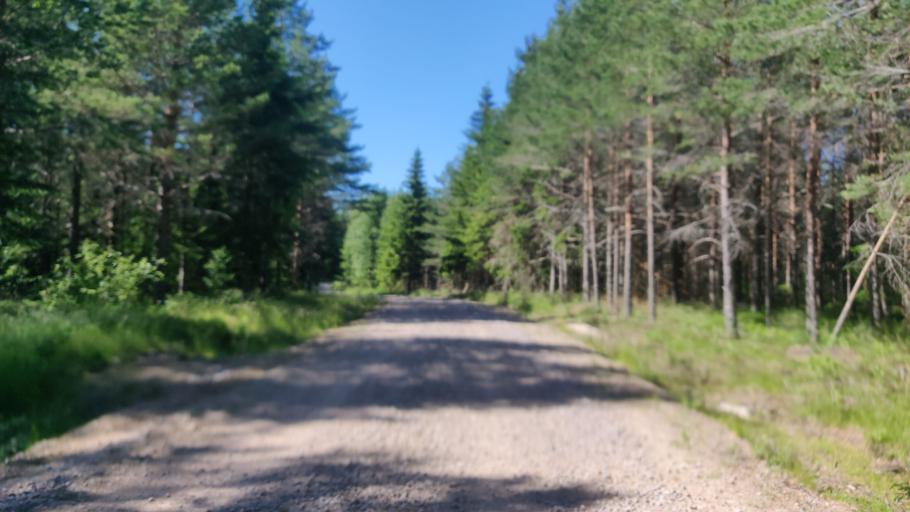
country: SE
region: Vaermland
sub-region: Hagfors Kommun
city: Hagfors
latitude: 59.9781
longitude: 13.6003
